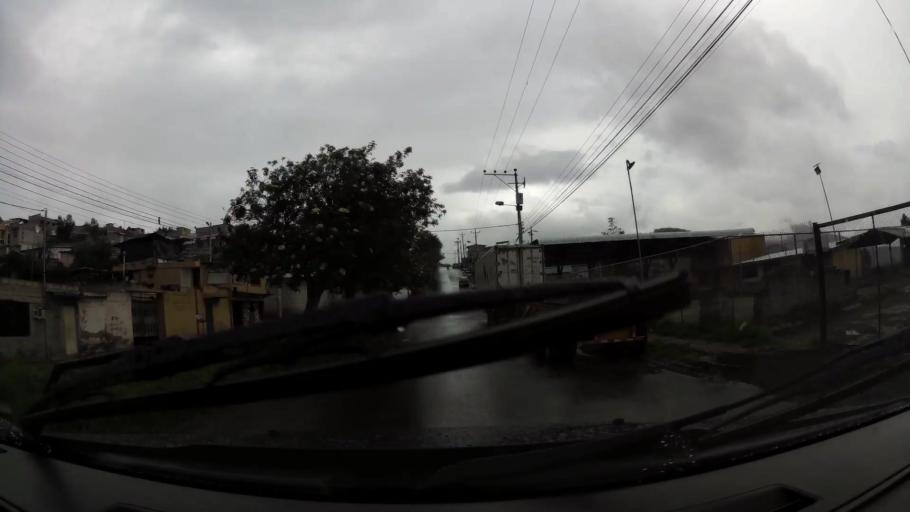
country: EC
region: Pichincha
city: Quito
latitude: -0.0905
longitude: -78.5122
